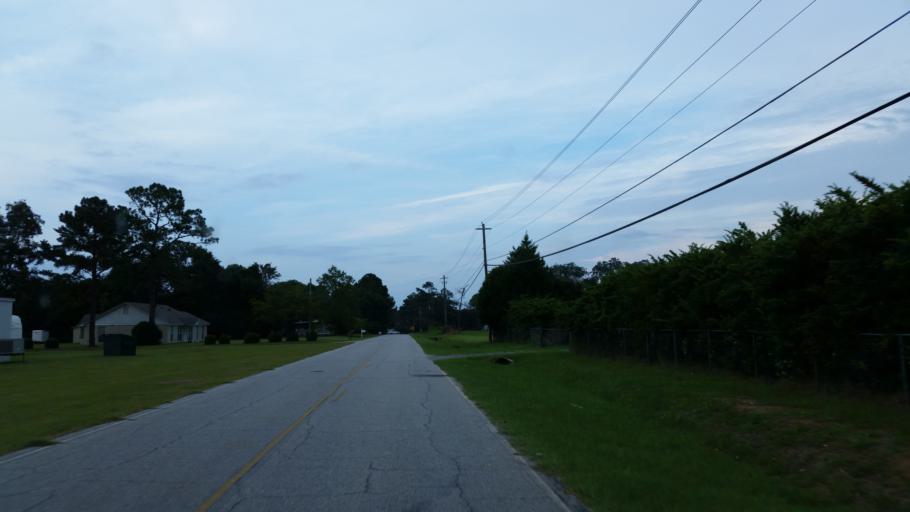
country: US
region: Georgia
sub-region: Lowndes County
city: Valdosta
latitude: 30.7619
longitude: -83.2673
